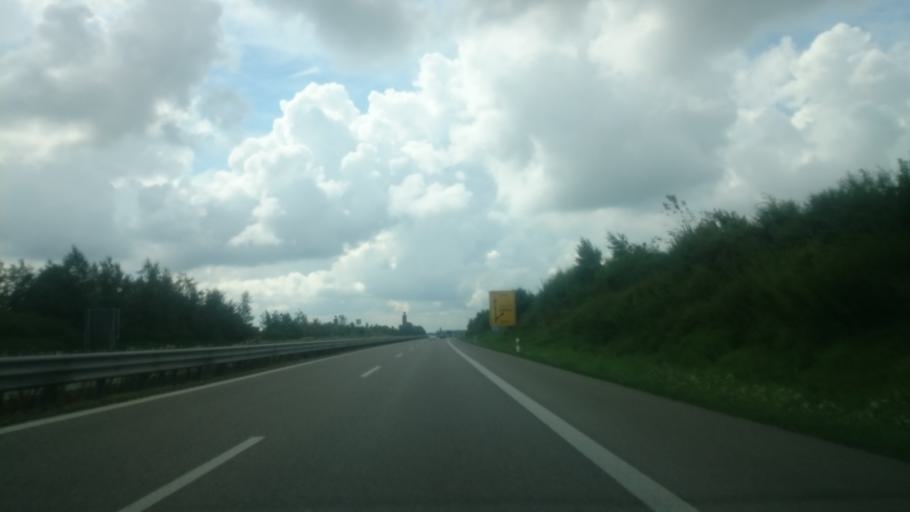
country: DE
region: Bavaria
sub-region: Upper Bavaria
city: Hurlach
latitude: 48.1346
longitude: 10.8322
